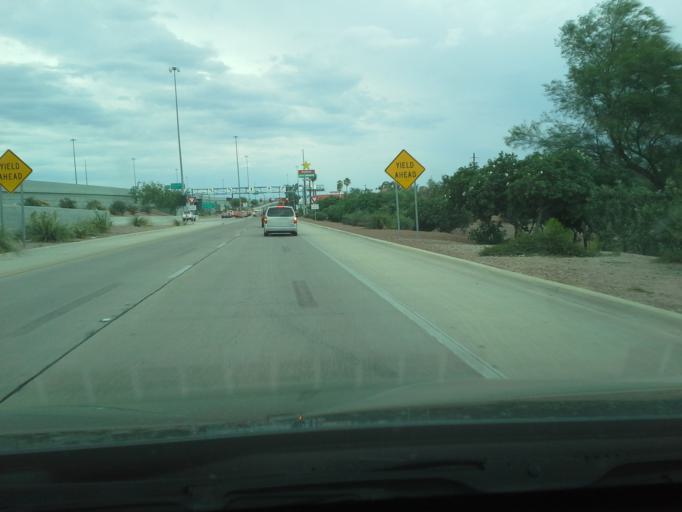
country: US
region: Arizona
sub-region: Pima County
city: South Tucson
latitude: 32.2230
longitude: -110.9811
